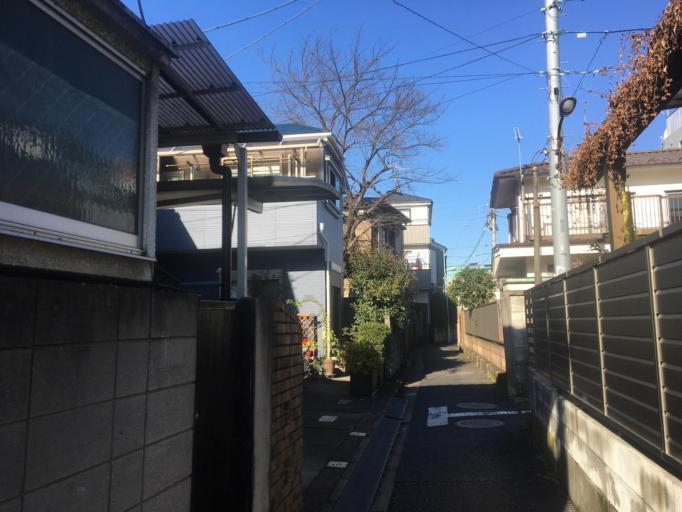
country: JP
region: Tokyo
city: Tokyo
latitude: 35.7378
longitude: 139.6983
